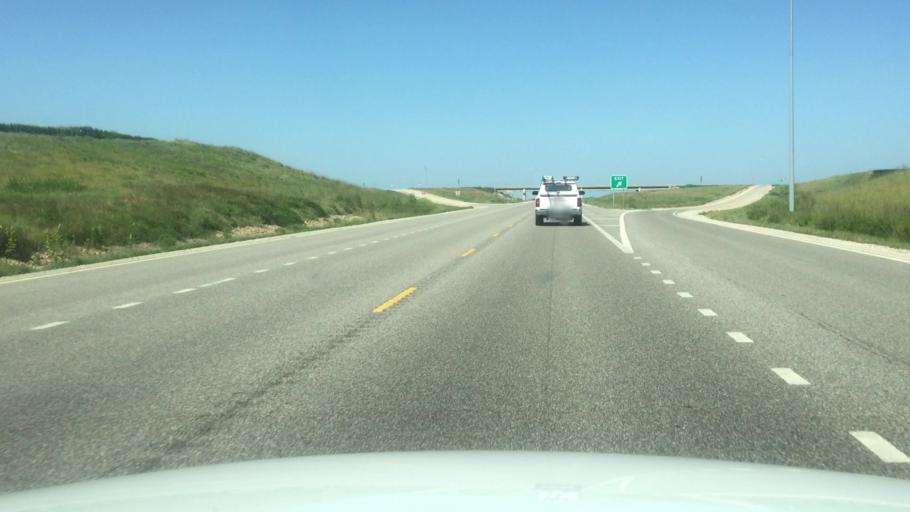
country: US
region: Kansas
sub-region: Doniphan County
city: Troy
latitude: 39.7979
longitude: -95.1377
